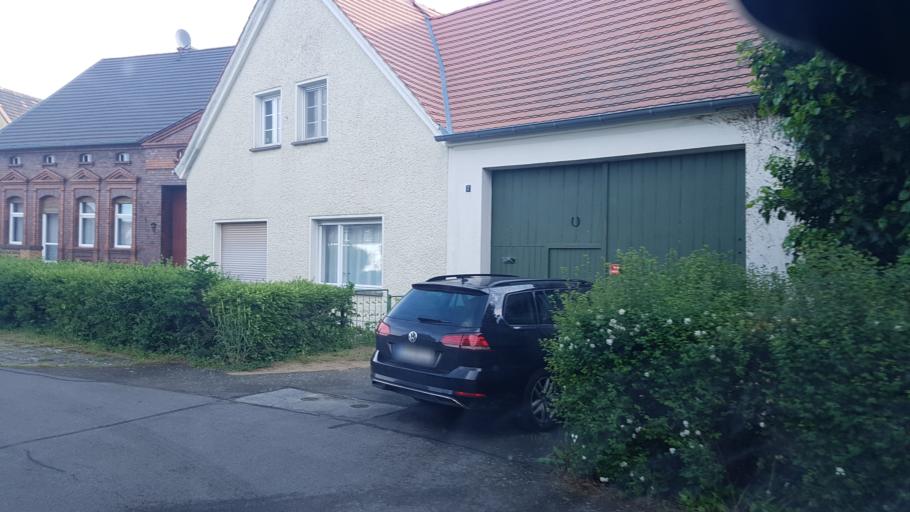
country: DE
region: Brandenburg
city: Luckau
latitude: 51.8304
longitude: 13.7445
